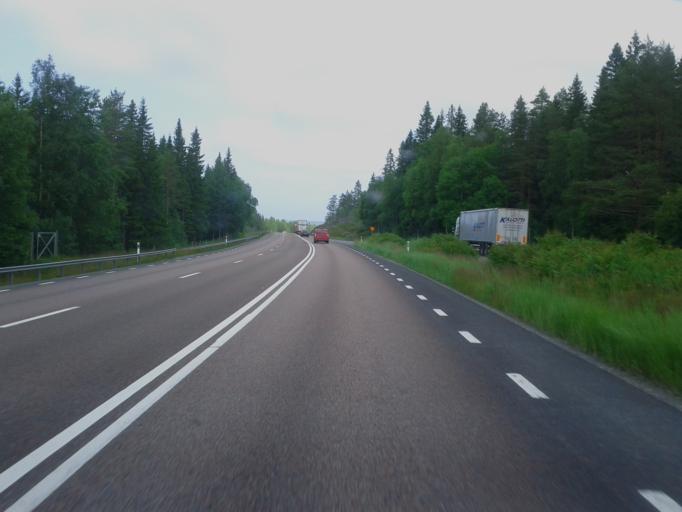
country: SE
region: Vaesterbotten
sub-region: Skelleftea Kommun
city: Burea
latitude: 64.4418
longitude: 21.2830
